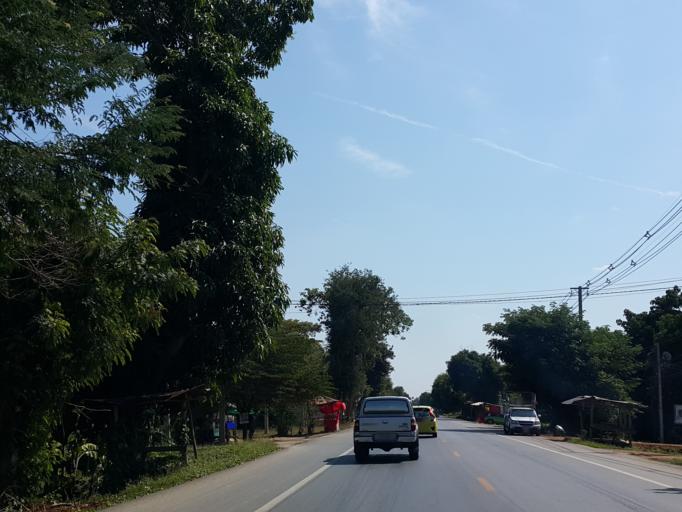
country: TH
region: Sukhothai
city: Sawankhalok
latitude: 17.2626
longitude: 99.8449
